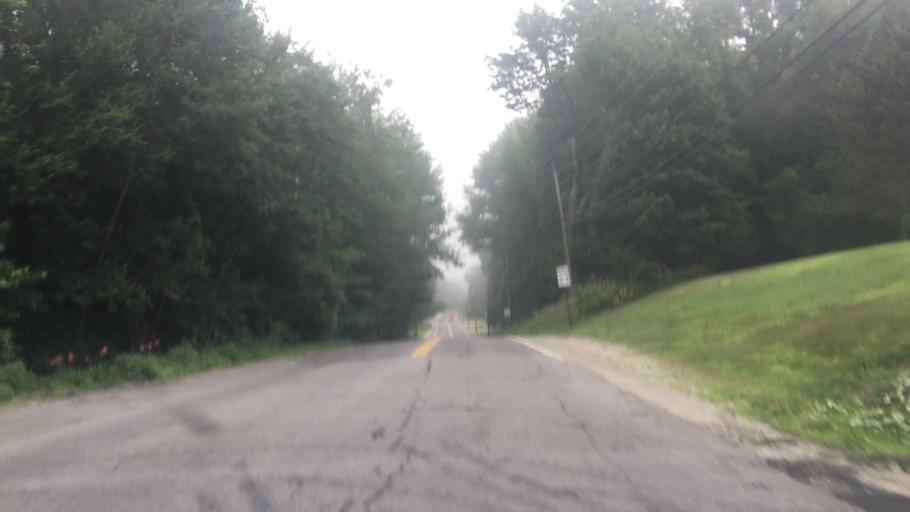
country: US
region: Maine
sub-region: Kennebec County
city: Oakland
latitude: 44.5320
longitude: -69.7239
